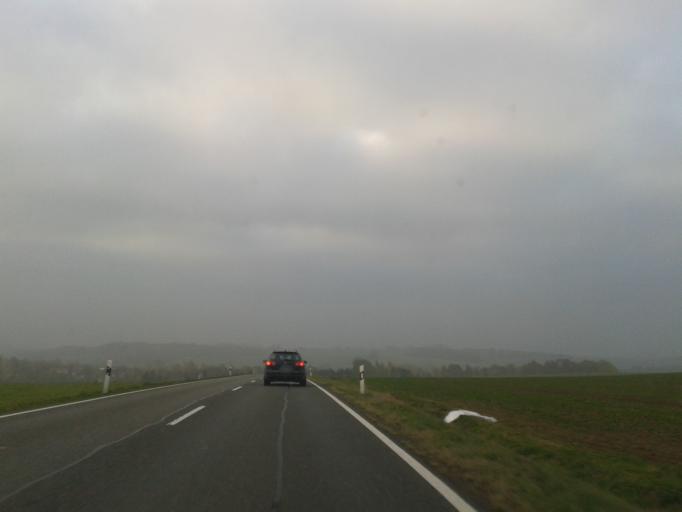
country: DE
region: Saxony
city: Niederschona
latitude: 50.9454
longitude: 13.4186
